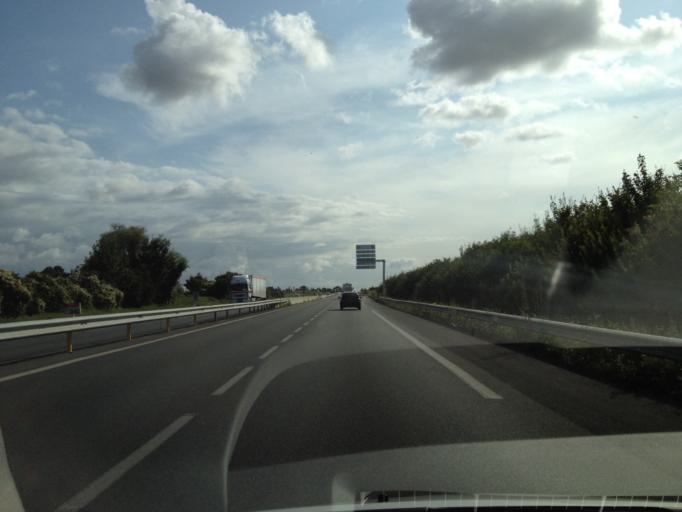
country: FR
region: Poitou-Charentes
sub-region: Departement de la Charente-Maritime
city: Puilboreau
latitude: 46.1793
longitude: -1.0957
